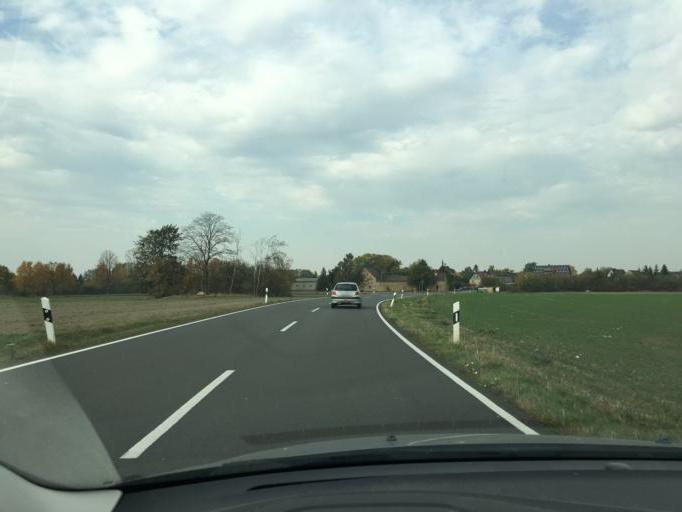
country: DE
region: Saxony
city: Zwochau
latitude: 51.4535
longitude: 12.2617
